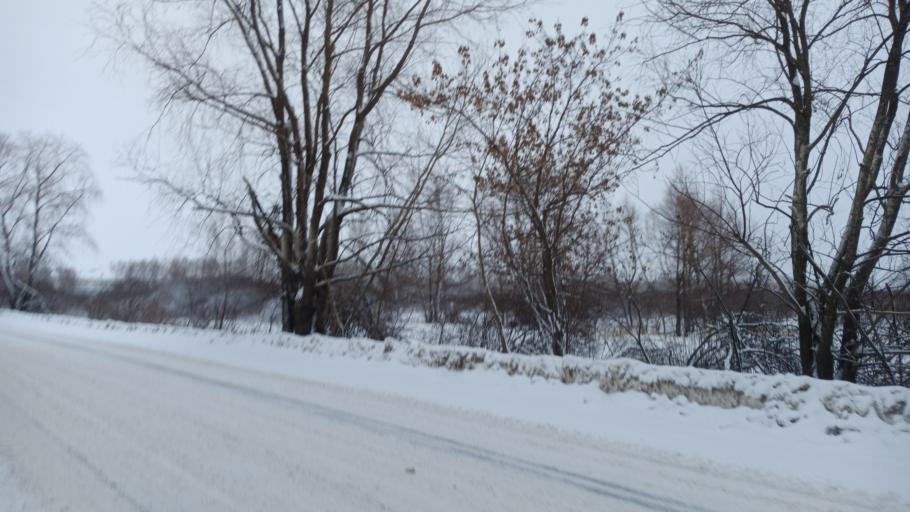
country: RU
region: Altai Krai
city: Zaton
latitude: 53.3114
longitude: 83.8306
